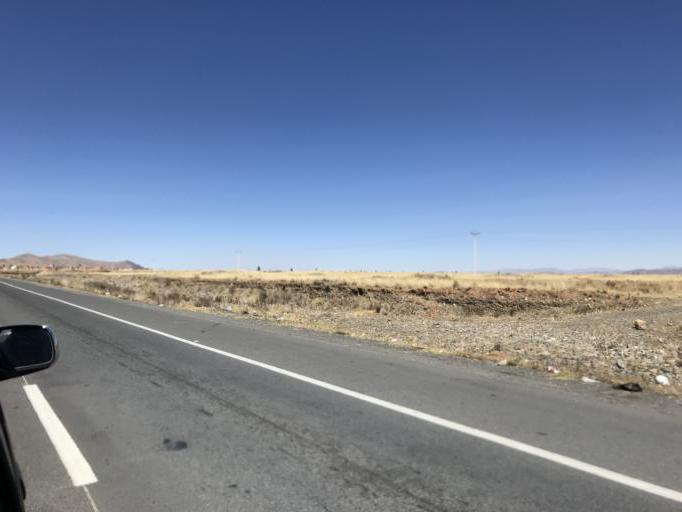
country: BO
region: La Paz
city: Batallas
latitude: -16.3207
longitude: -68.4357
